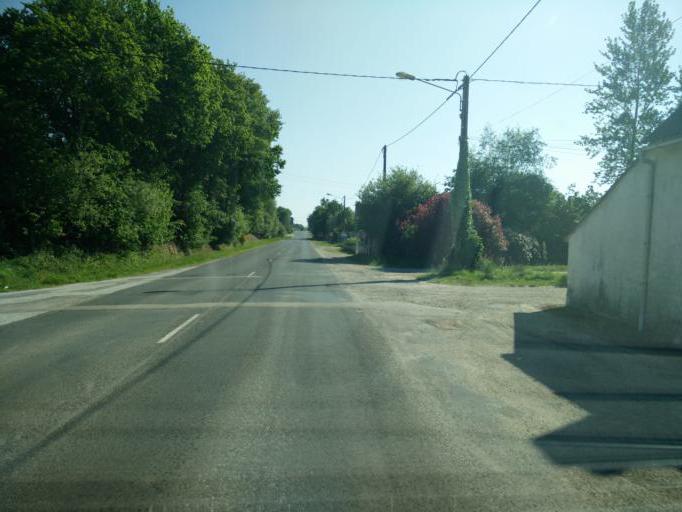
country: FR
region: Brittany
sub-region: Departement du Morbihan
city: Branderion
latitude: 47.8225
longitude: -3.2048
